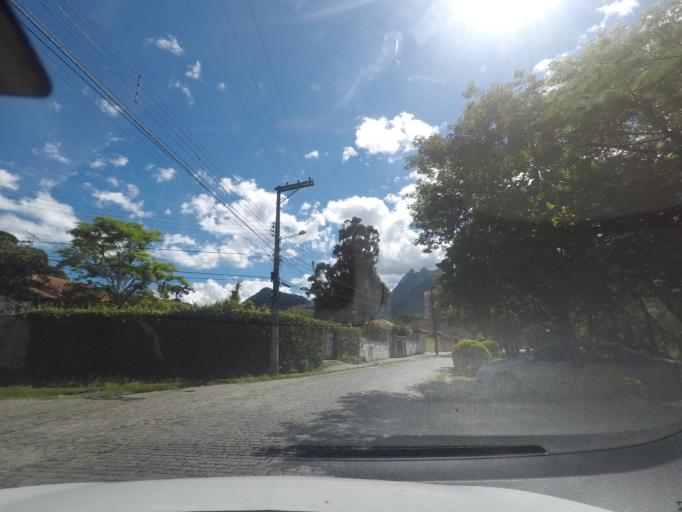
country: BR
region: Rio de Janeiro
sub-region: Teresopolis
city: Teresopolis
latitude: -22.4363
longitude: -42.9751
